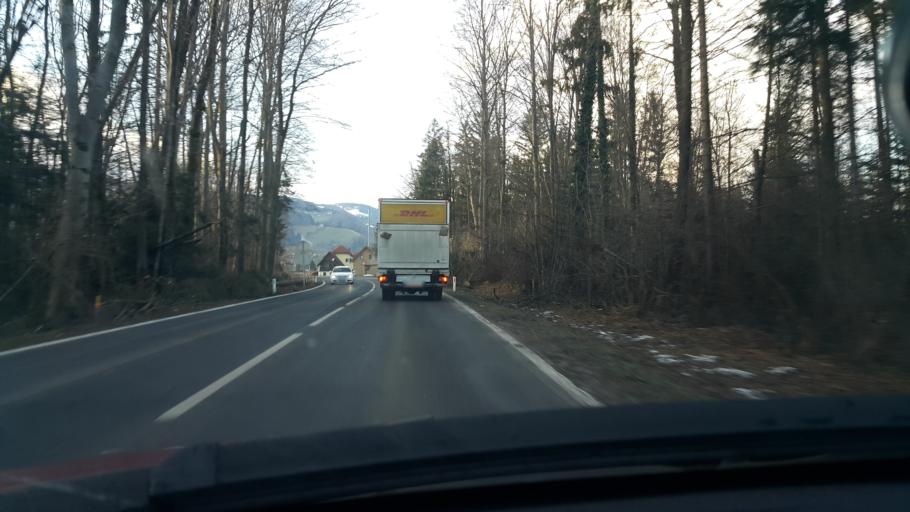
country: AT
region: Styria
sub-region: Politischer Bezirk Deutschlandsberg
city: Hollenegg
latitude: 46.7989
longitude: 15.2239
